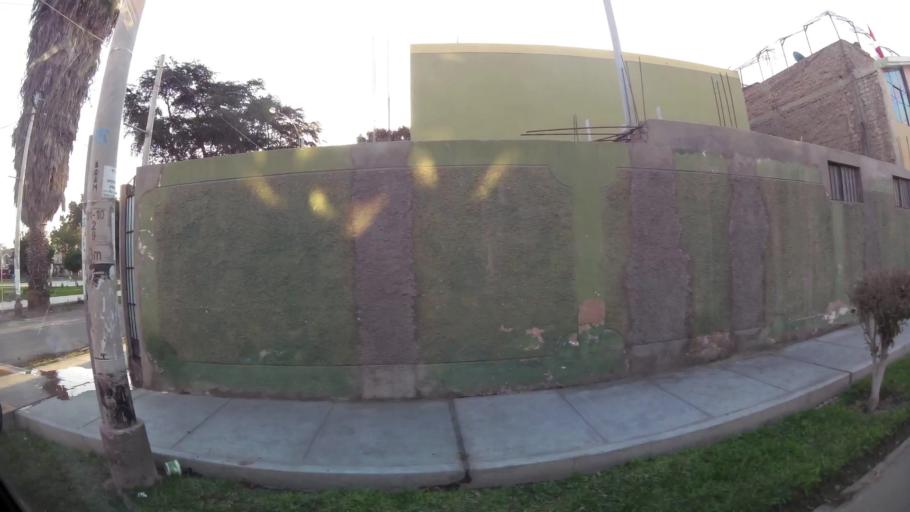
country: PE
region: Ica
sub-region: Provincia de Ica
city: Ica
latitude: -14.0861
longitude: -75.7240
